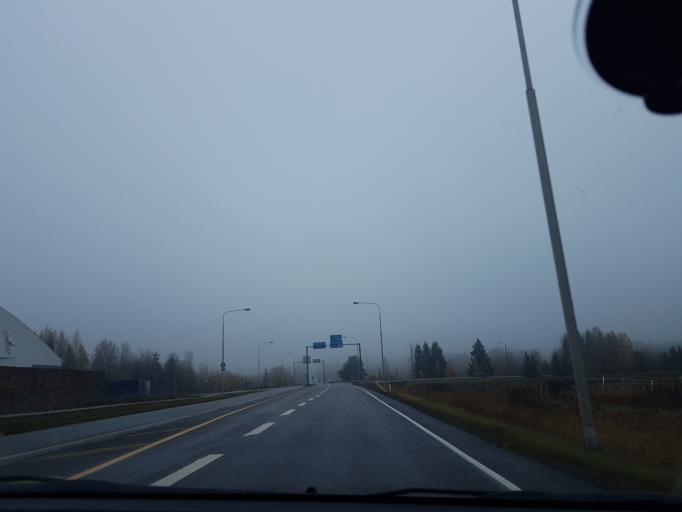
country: FI
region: Uusimaa
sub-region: Helsinki
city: Jaervenpaeae
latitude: 60.4687
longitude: 25.1413
